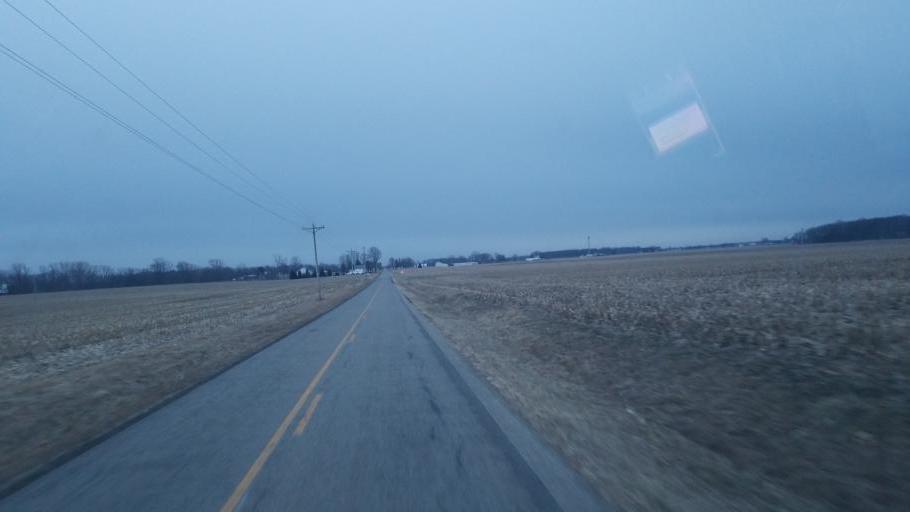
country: US
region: Ohio
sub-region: Defiance County
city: Hicksville
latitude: 41.3272
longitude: -84.7285
